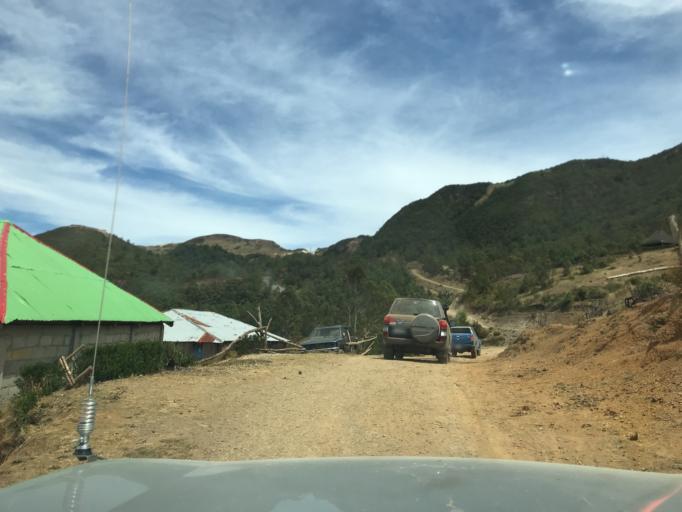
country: TL
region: Ainaro
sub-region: Ainaro
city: Ainaro
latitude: -8.8805
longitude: 125.5332
